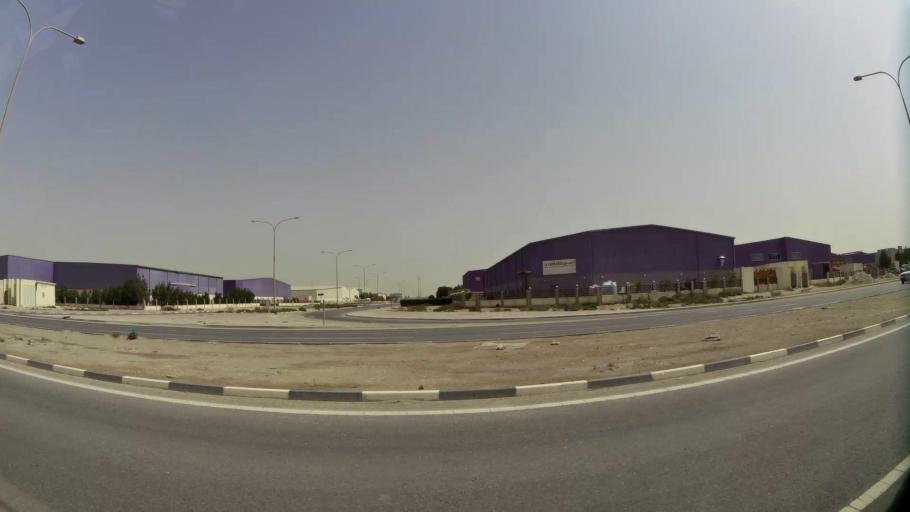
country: QA
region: Baladiyat ar Rayyan
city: Ar Rayyan
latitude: 25.1623
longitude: 51.4061
